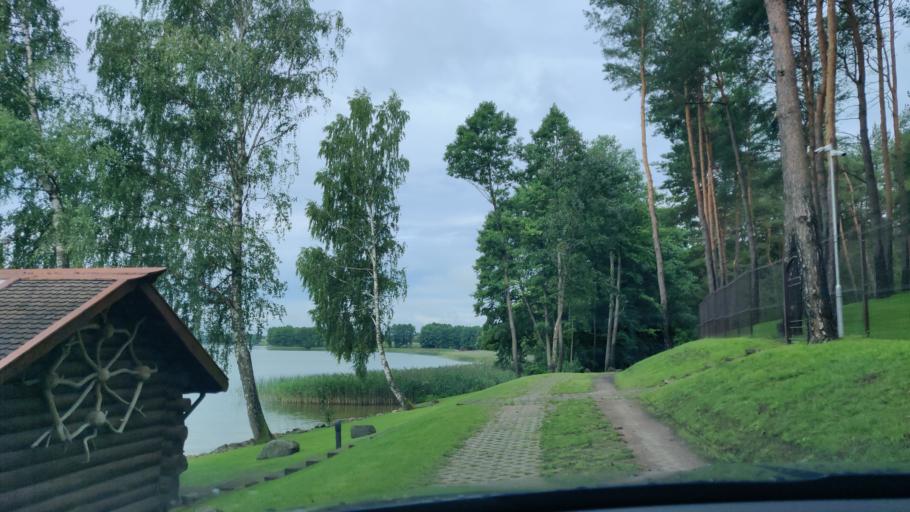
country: LT
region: Vilnius County
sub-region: Trakai
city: Rudiskes
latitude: 54.6096
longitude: 24.8282
